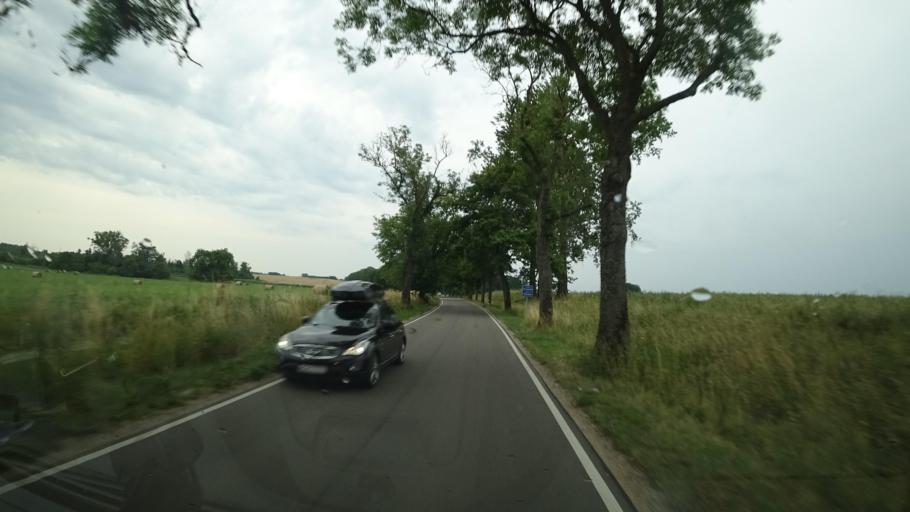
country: PL
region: Warmian-Masurian Voivodeship
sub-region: Powiat mragowski
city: Mikolajki
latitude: 53.8672
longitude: 21.5973
